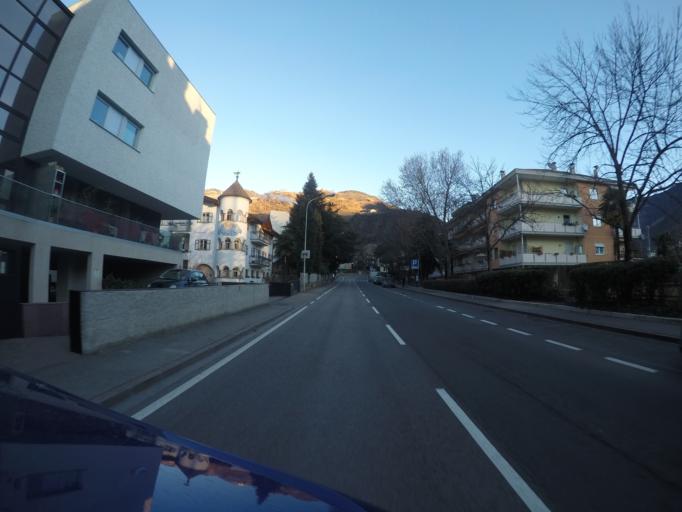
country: IT
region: Trentino-Alto Adige
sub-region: Bolzano
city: Bolzano
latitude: 46.5078
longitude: 11.3471
